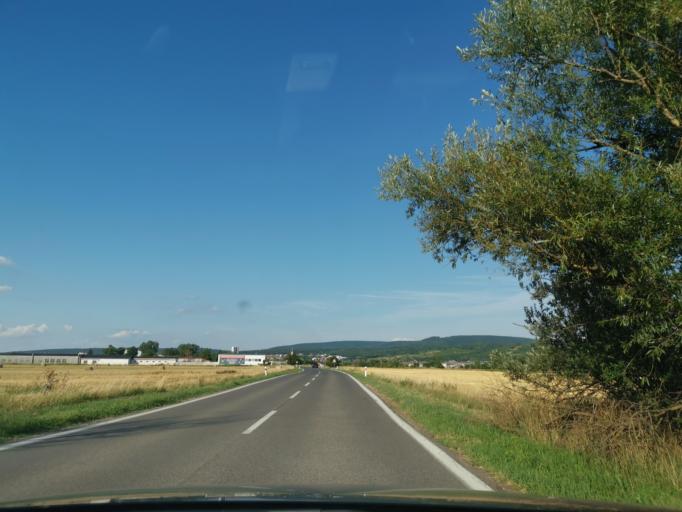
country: SK
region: Bratislavsky
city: Stupava
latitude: 48.2578
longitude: 17.0150
